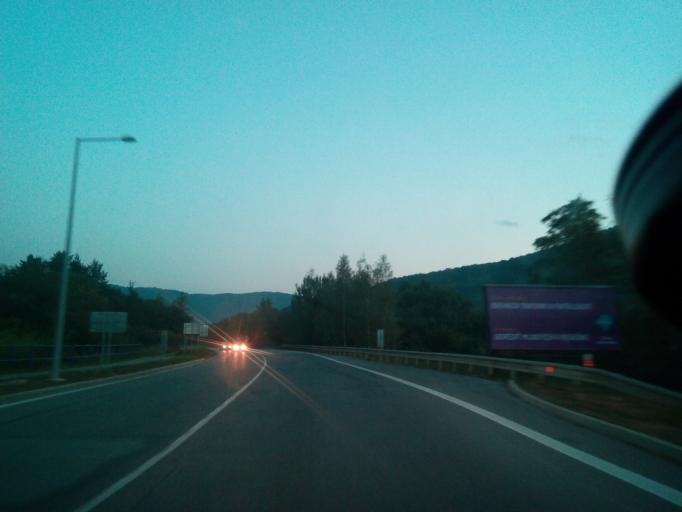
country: SK
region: Kosicky
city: Roznava
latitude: 48.6593
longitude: 20.5205
